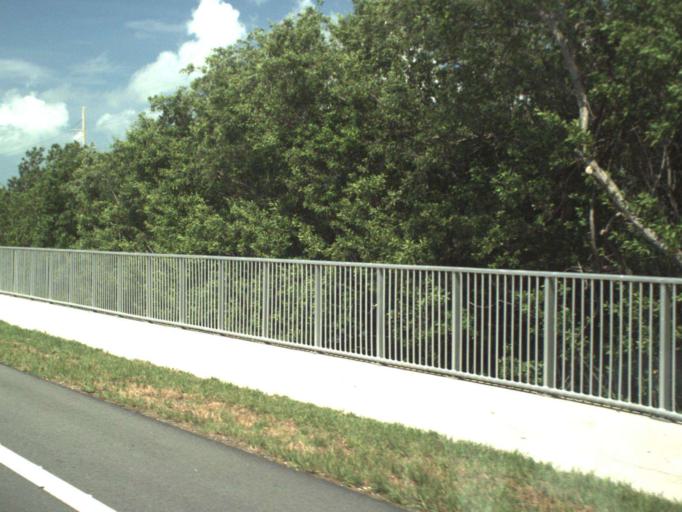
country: US
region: Florida
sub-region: Monroe County
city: Islamorada
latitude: 24.8498
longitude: -80.7398
